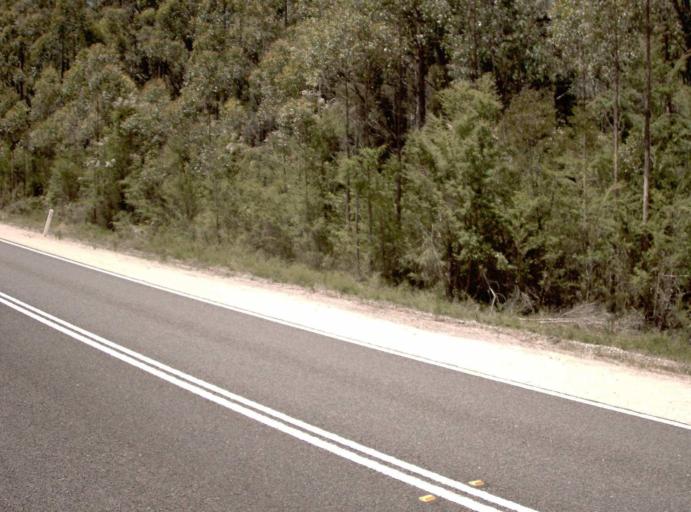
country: AU
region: New South Wales
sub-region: Bombala
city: Bombala
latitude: -37.6244
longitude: 148.8897
